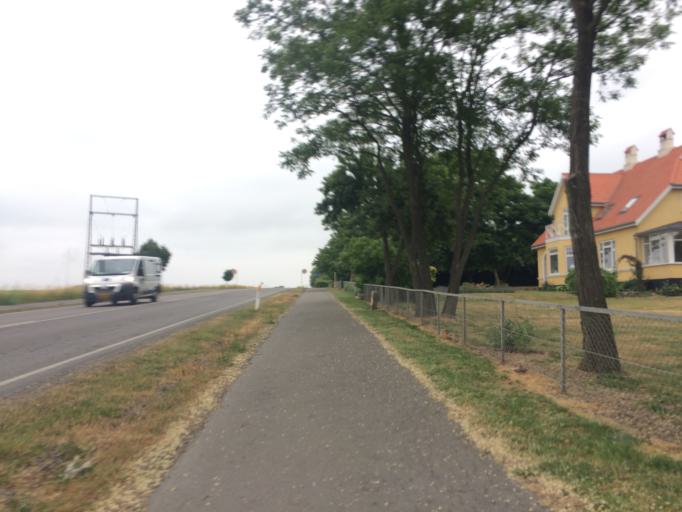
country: DK
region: Capital Region
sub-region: Bornholm Kommune
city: Ronne
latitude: 55.1061
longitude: 14.7376
